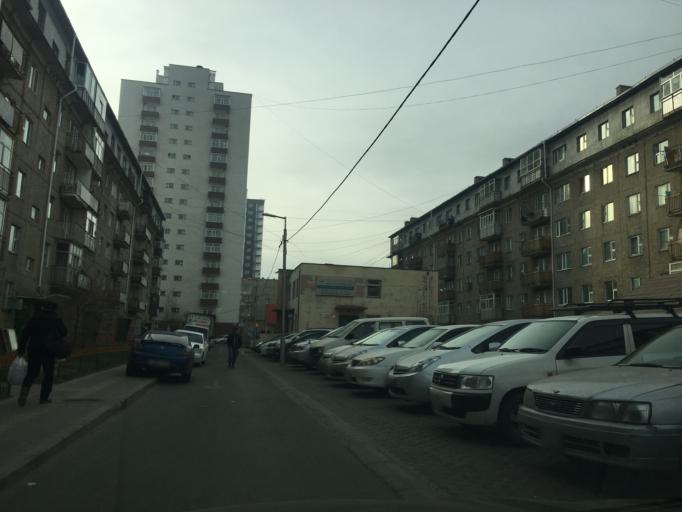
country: MN
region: Ulaanbaatar
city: Ulaanbaatar
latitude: 47.9120
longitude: 106.8879
